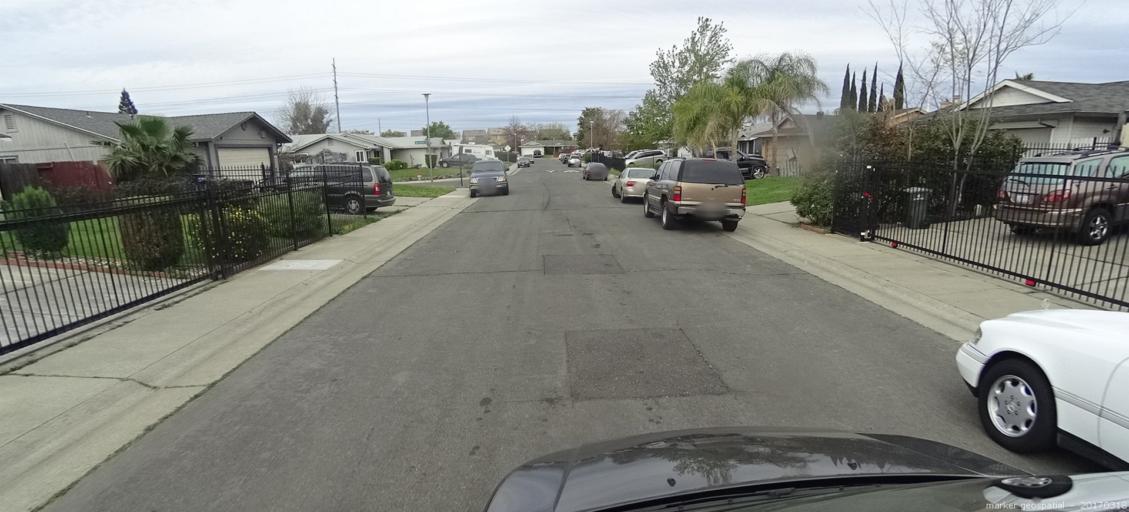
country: US
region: California
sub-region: Sacramento County
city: Parkway
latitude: 38.4884
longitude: -121.4661
